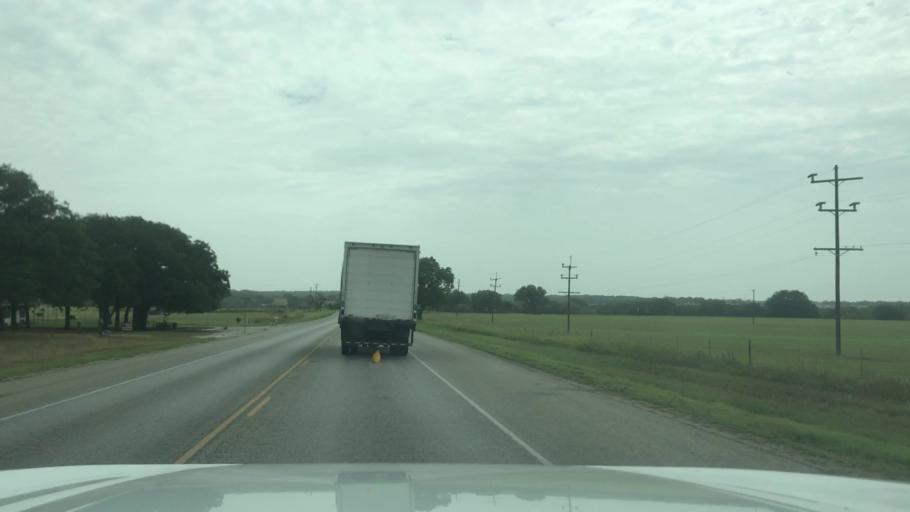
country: US
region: Texas
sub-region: Comanche County
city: De Leon
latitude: 32.0961
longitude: -98.4590
